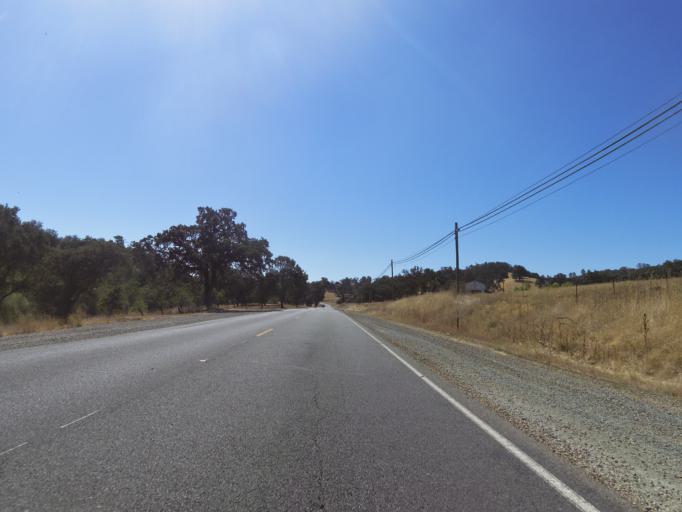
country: US
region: California
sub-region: Amador County
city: Plymouth
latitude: 38.4967
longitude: -120.8483
